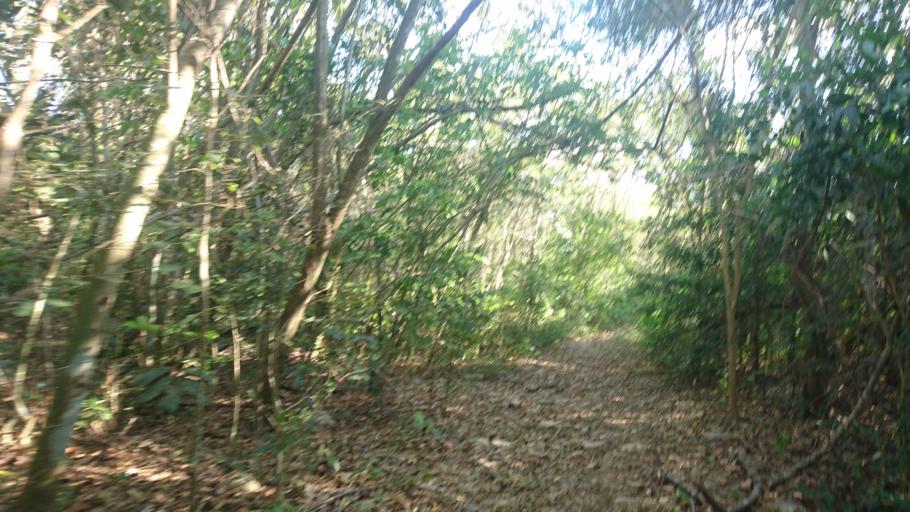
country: CU
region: Artemisa
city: Soroa
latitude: 22.8289
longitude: -82.9209
